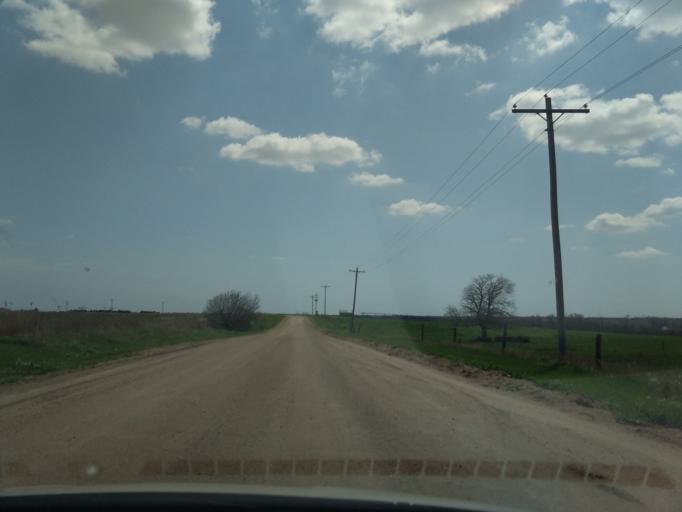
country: US
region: Nebraska
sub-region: Thayer County
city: Hebron
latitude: 40.3350
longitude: -97.4389
